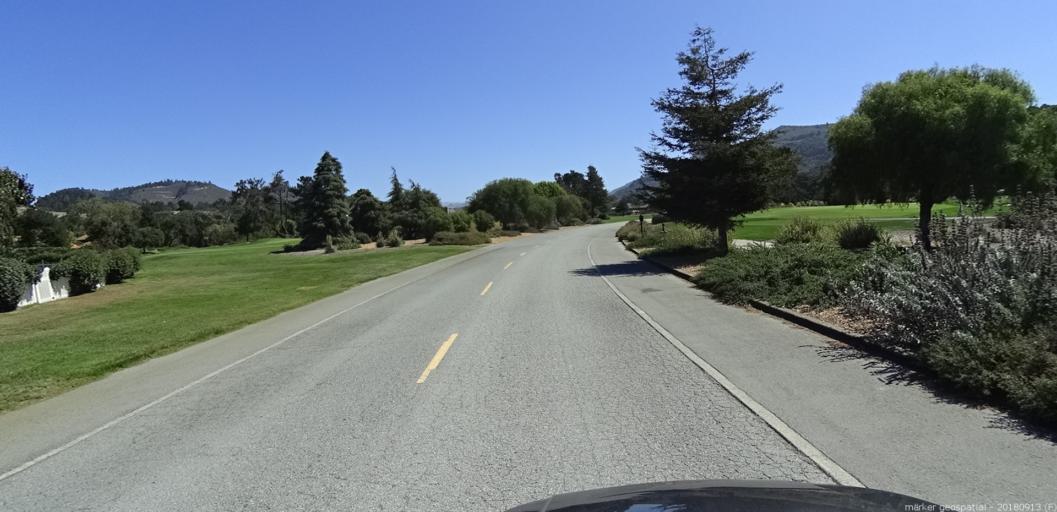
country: US
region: California
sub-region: Monterey County
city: Carmel-by-the-Sea
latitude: 36.5327
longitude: -121.8645
